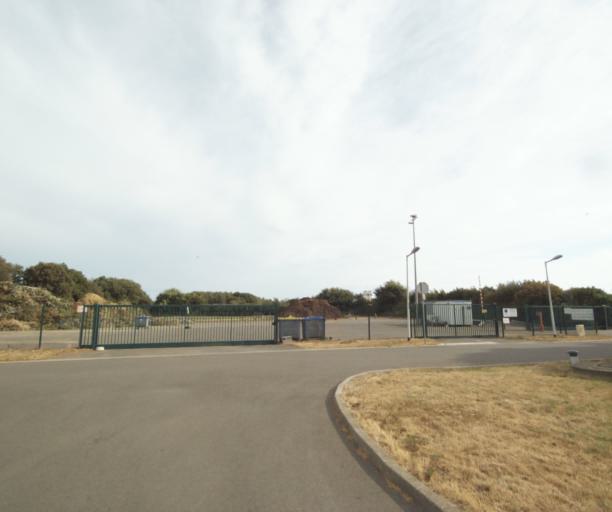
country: FR
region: Pays de la Loire
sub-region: Departement de la Vendee
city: Chateau-d'Olonne
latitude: 46.4923
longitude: -1.7234
